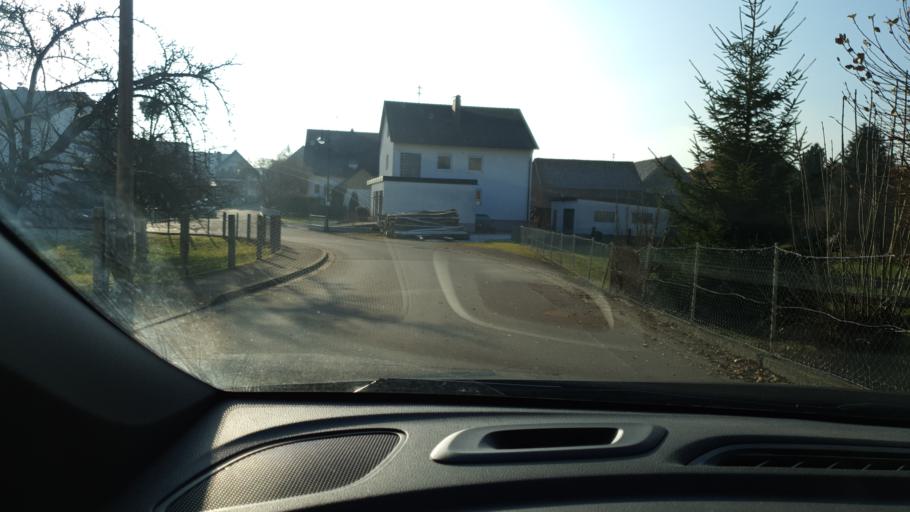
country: DE
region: Bavaria
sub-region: Swabia
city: Burgau
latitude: 48.4311
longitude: 10.3973
